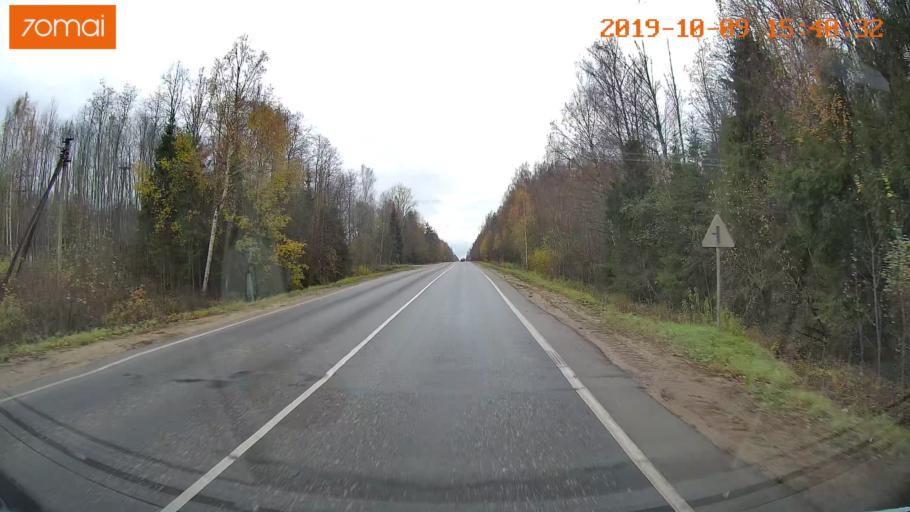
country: RU
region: Kostroma
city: Oktyabr'skiy
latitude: 57.8867
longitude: 41.1425
